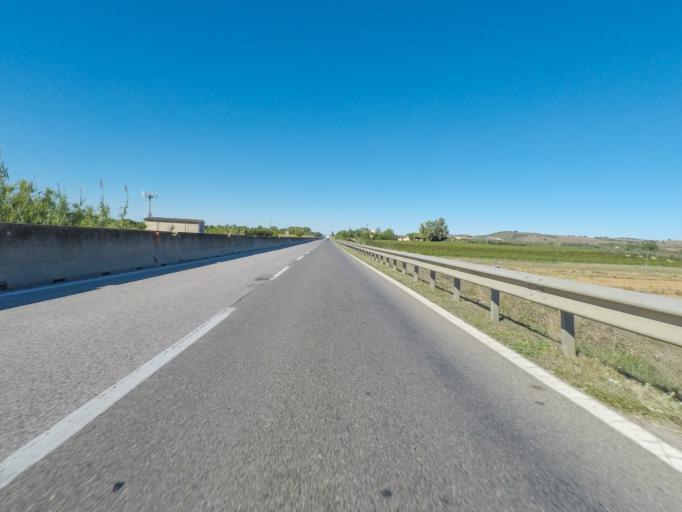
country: IT
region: Tuscany
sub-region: Provincia di Grosseto
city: Grosseto
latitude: 42.6832
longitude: 11.1398
